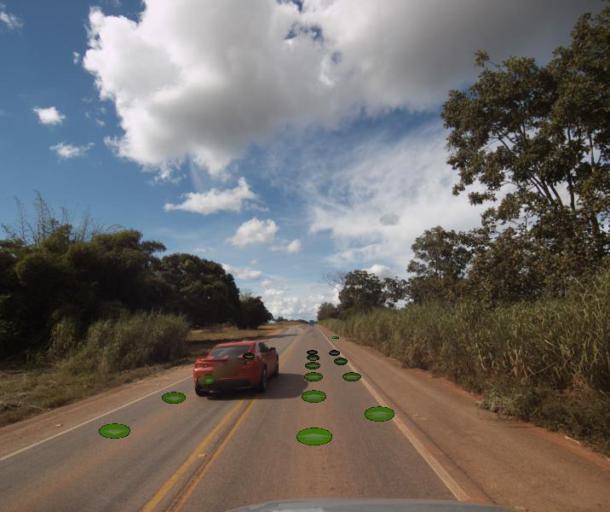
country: BR
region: Goias
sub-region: Porangatu
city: Porangatu
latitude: -13.1055
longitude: -49.2000
